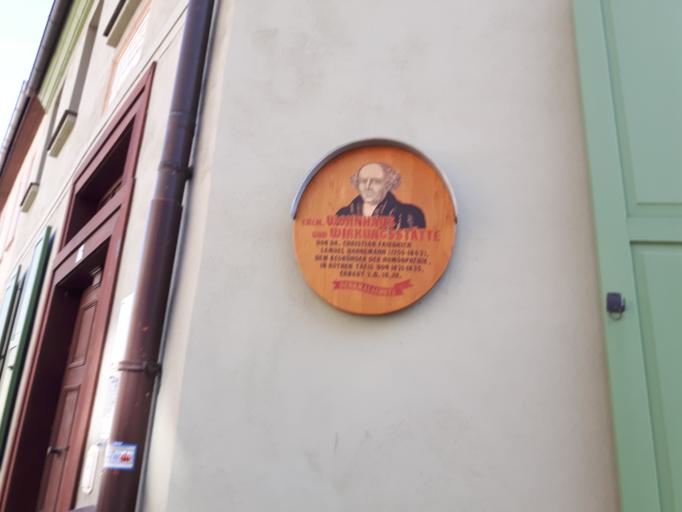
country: DE
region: Saxony-Anhalt
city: Koethen
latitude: 51.7533
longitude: 11.9703
